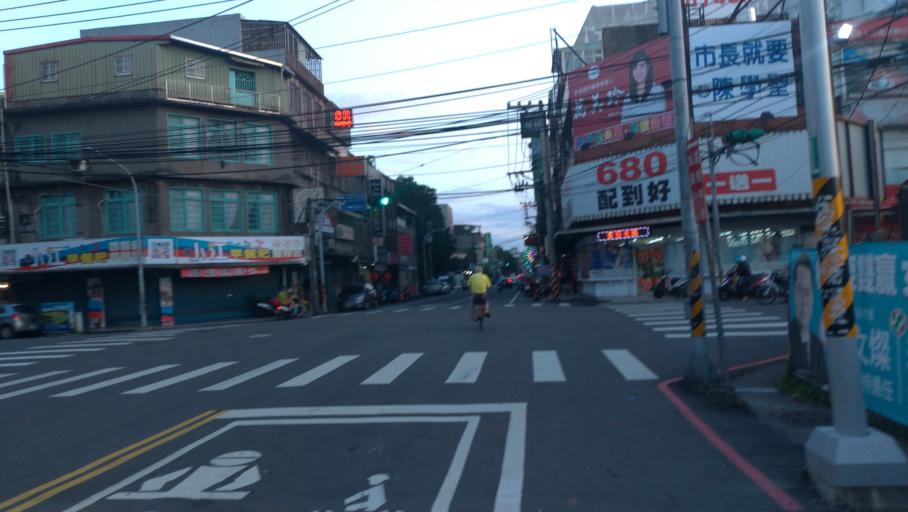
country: TW
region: Taiwan
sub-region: Taoyuan
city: Taoyuan
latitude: 24.9859
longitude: 121.3143
